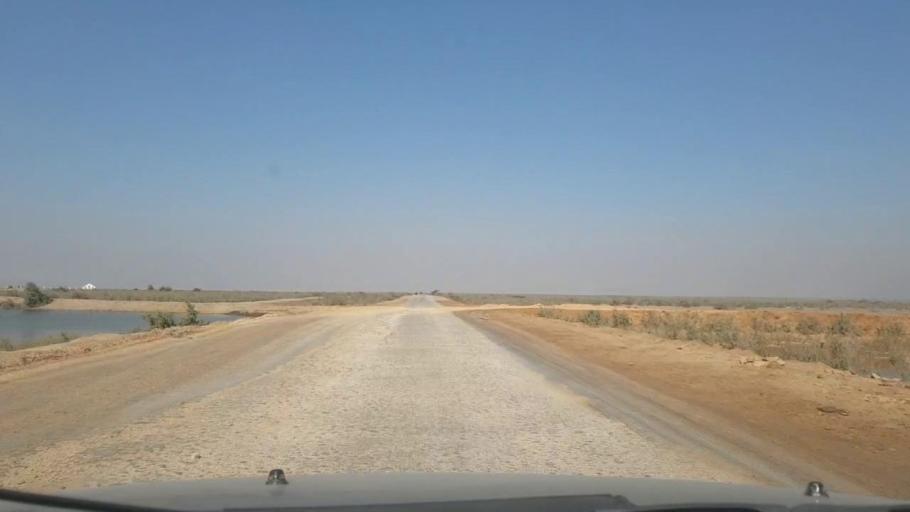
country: PK
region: Sindh
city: Thatta
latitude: 24.8157
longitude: 67.8964
